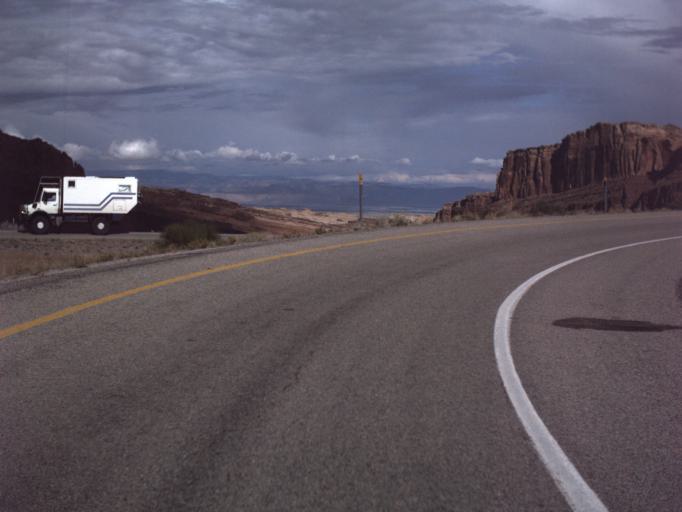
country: US
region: Utah
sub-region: Emery County
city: Castle Dale
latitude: 38.9393
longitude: -110.4820
